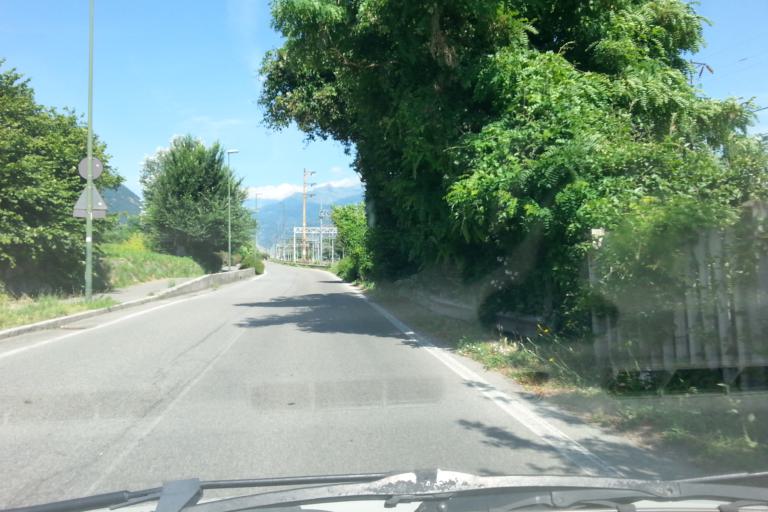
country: IT
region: Piedmont
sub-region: Provincia di Torino
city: Avigliana
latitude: 45.0869
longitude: 7.3950
